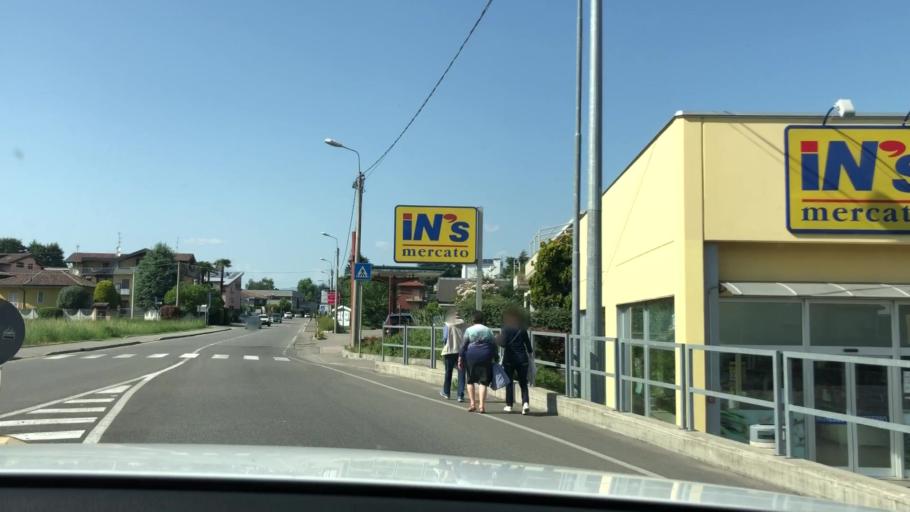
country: IT
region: Lombardy
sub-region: Provincia di Como
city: Cadorago-Caslino al Piano
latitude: 45.7158
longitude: 9.0394
